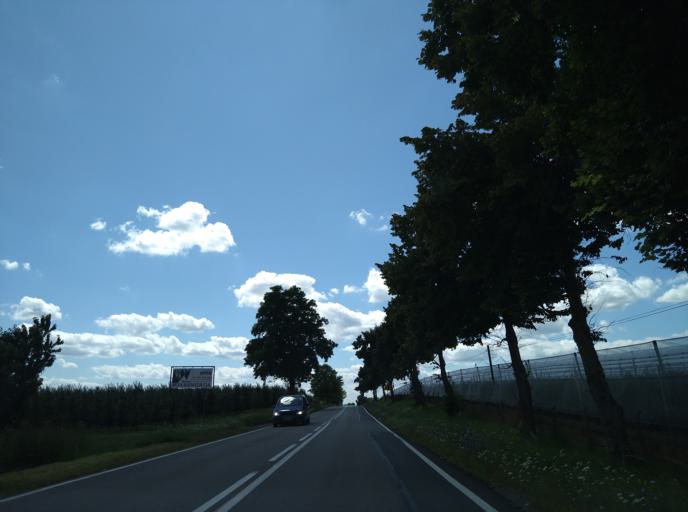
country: PL
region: Masovian Voivodeship
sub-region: Powiat bialobrzeski
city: Stromiec
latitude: 51.7349
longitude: 21.0804
